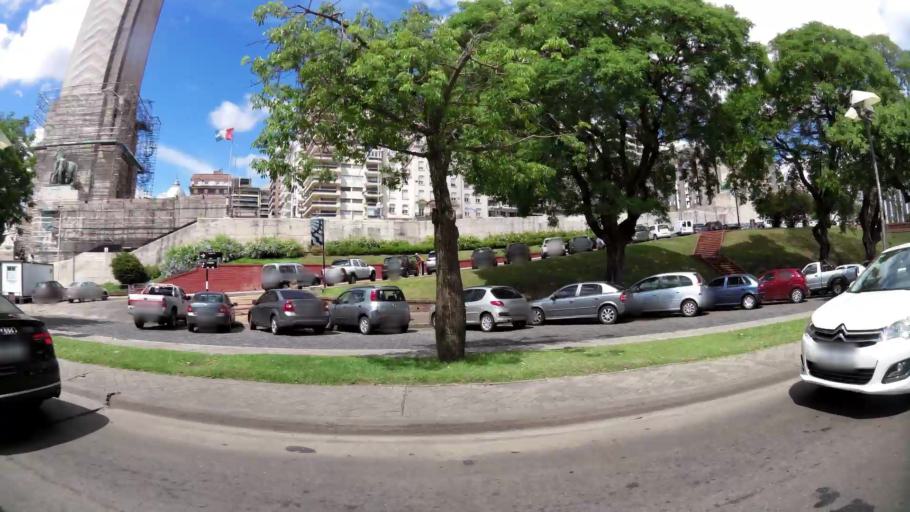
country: AR
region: Santa Fe
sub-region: Departamento de Rosario
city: Rosario
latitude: -32.9473
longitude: -60.6299
